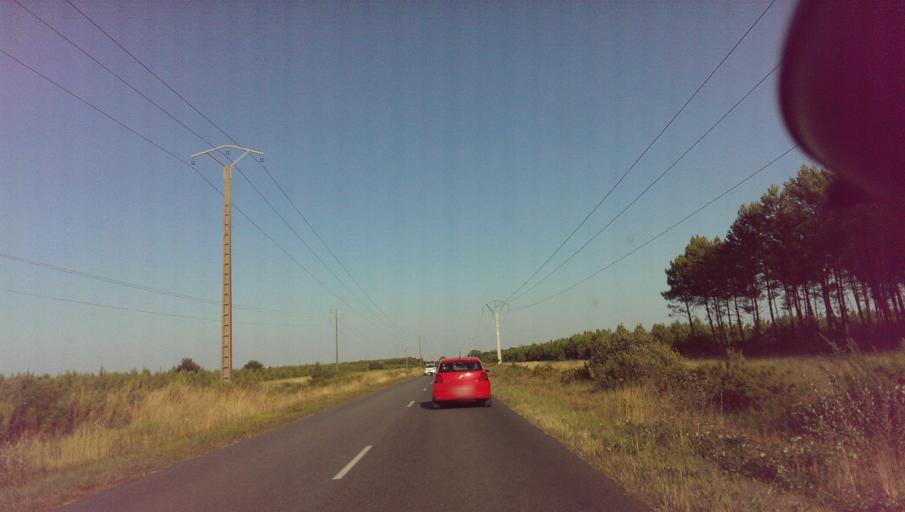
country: FR
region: Aquitaine
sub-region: Departement des Landes
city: Mimizan
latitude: 44.1845
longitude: -1.1921
